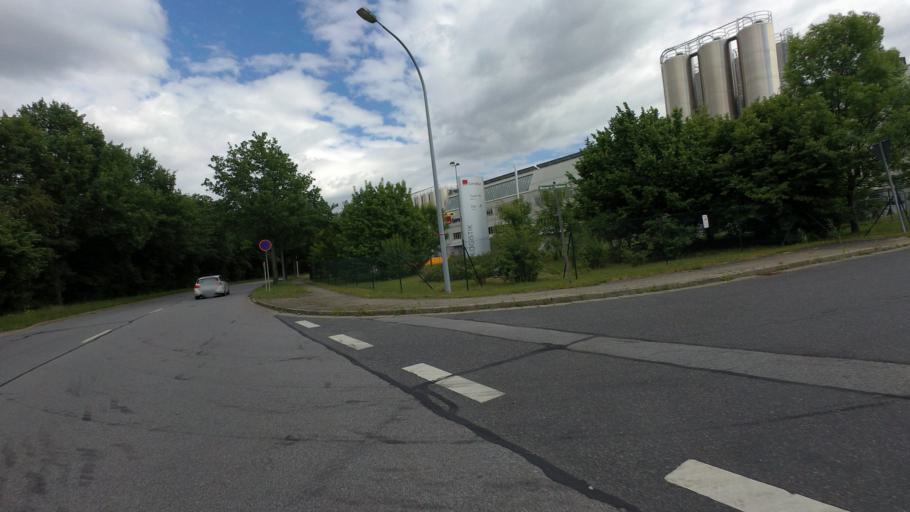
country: DE
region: Saxony
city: Neustadt in Sachsen
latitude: 51.0363
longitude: 14.2237
